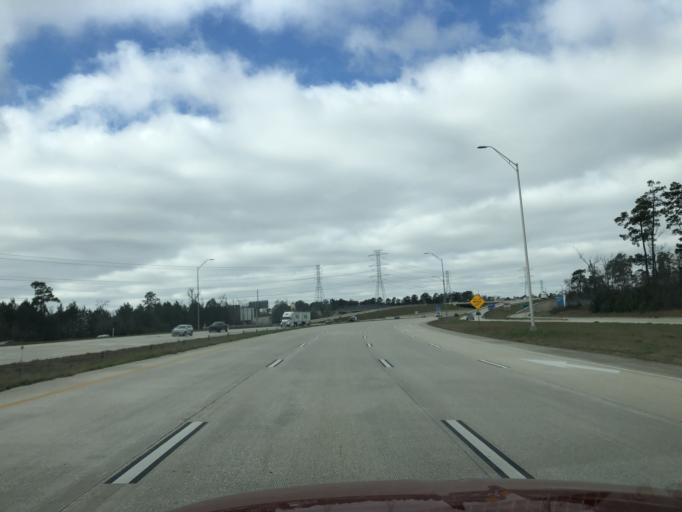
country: US
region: Texas
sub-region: Harris County
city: Spring
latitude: 30.0886
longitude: -95.4458
